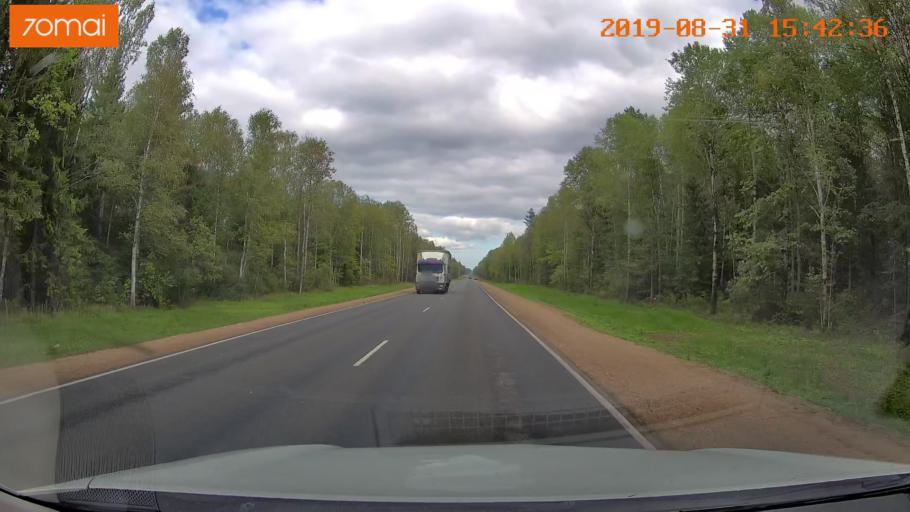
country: RU
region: Kaluga
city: Mosal'sk
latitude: 54.6473
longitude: 34.8900
